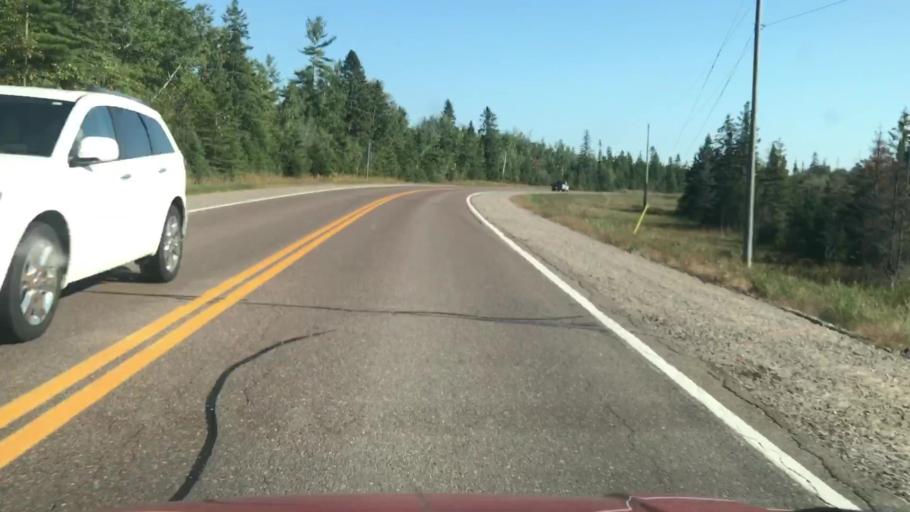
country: CA
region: Ontario
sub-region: Algoma
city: Sault Ste. Marie
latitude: 46.3354
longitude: -84.0069
